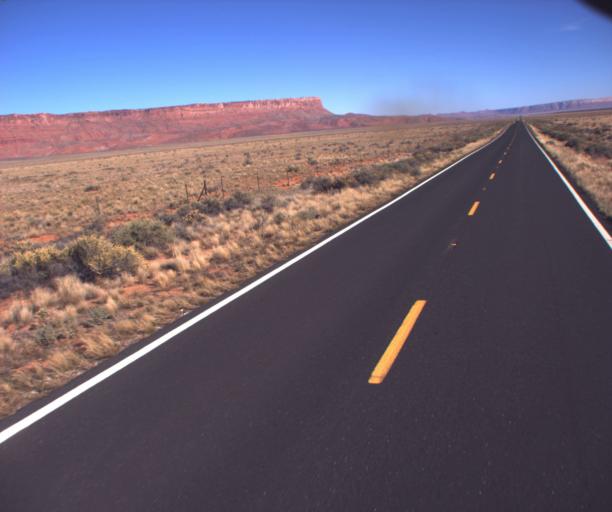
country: US
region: Arizona
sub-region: Coconino County
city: Page
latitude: 36.7074
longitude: -111.9579
